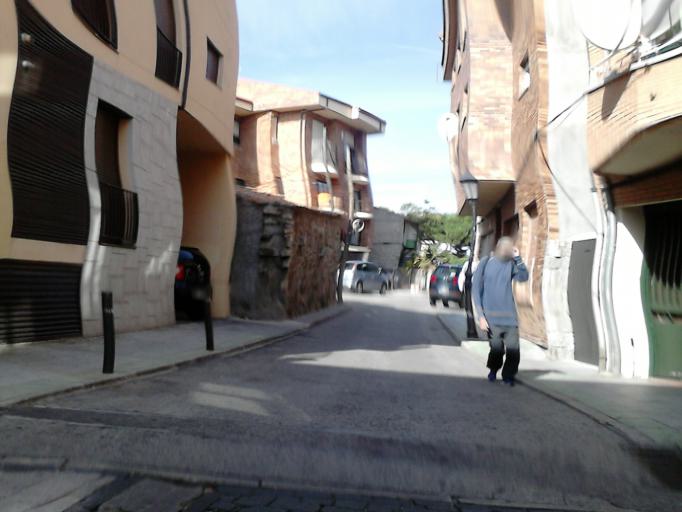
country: ES
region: Madrid
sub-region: Provincia de Madrid
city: Galapagar
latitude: 40.5792
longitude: -4.0036
